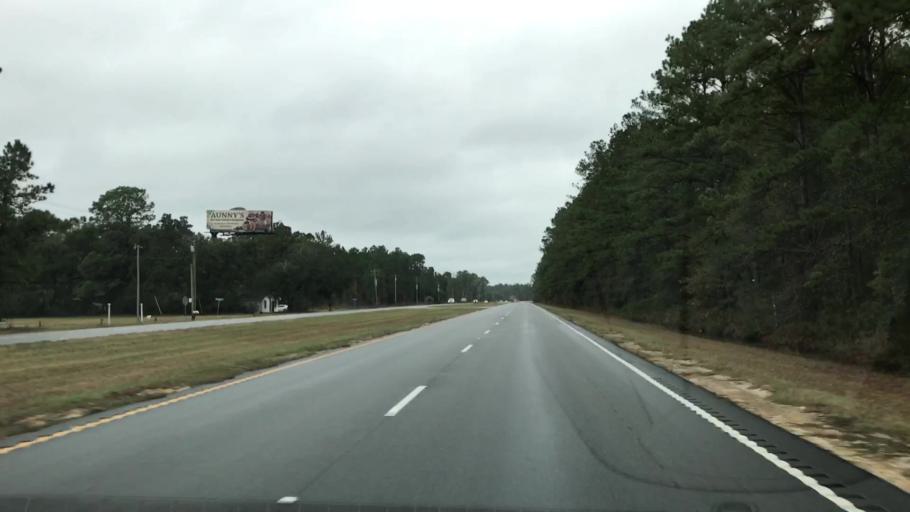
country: US
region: South Carolina
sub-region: Georgetown County
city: Georgetown
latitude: 33.2397
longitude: -79.3756
